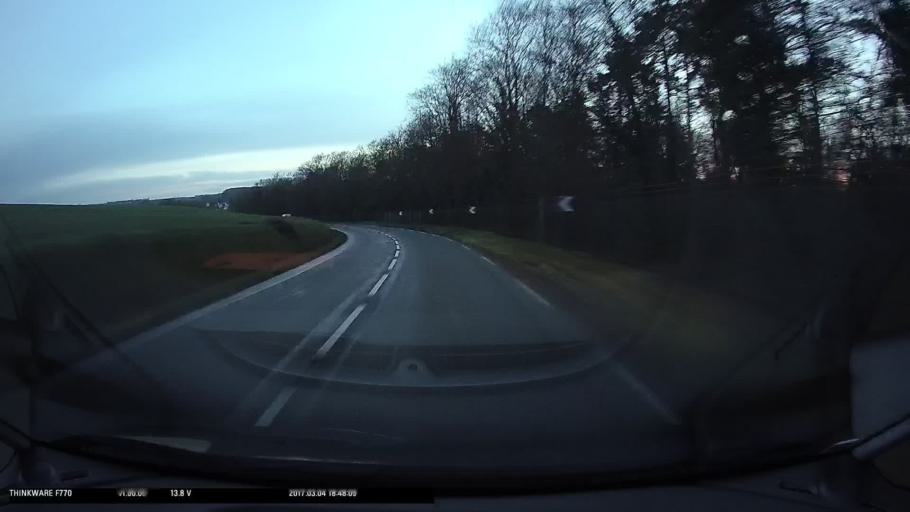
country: FR
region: Ile-de-France
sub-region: Departement du Val-d'Oise
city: Us
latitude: 49.1074
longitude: 1.9727
